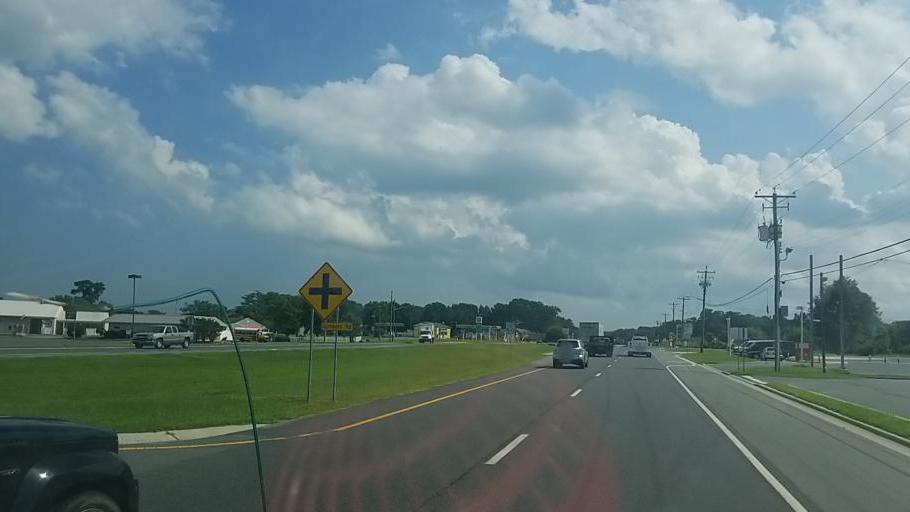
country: US
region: Delaware
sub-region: Sussex County
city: Selbyville
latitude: 38.4591
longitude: -75.2338
